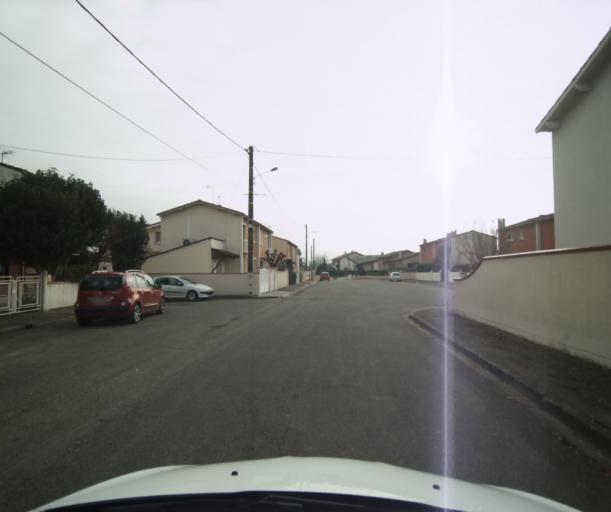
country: FR
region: Midi-Pyrenees
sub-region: Departement du Tarn-et-Garonne
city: Castelsarrasin
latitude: 44.0328
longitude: 1.1158
